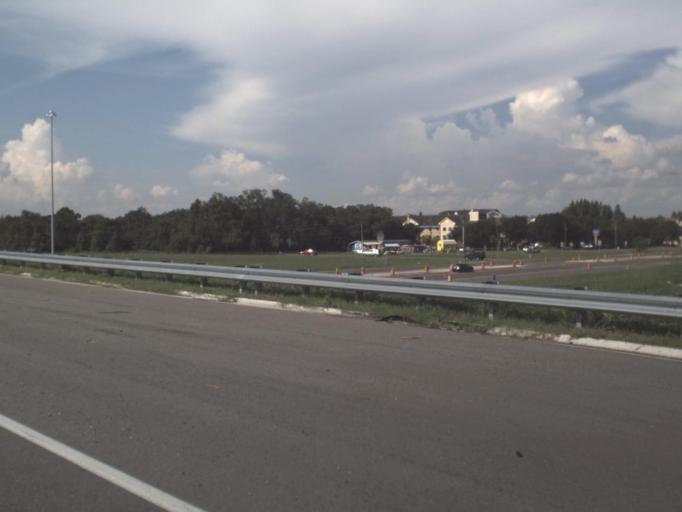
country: US
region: Florida
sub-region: Hillsborough County
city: Temple Terrace
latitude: 28.0707
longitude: -82.3541
